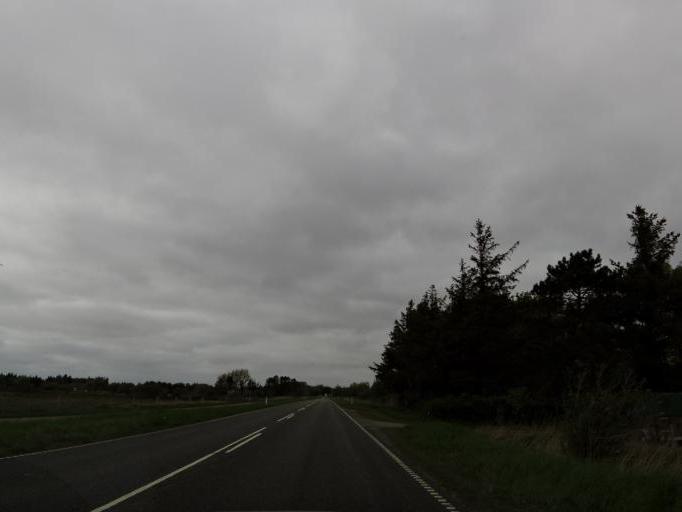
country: DE
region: Schleswig-Holstein
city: List
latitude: 55.1364
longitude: 8.5489
